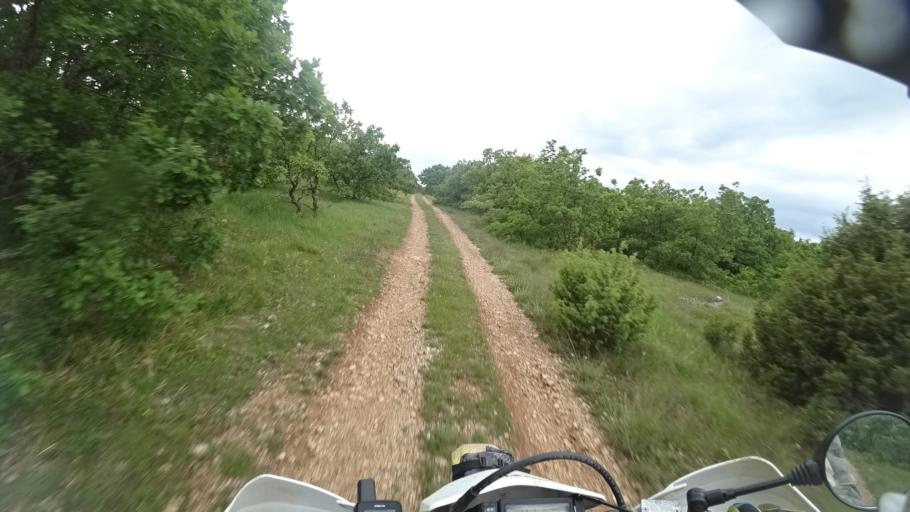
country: HR
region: Sibensko-Kniniska
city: Knin
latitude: 43.9854
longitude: 16.3303
